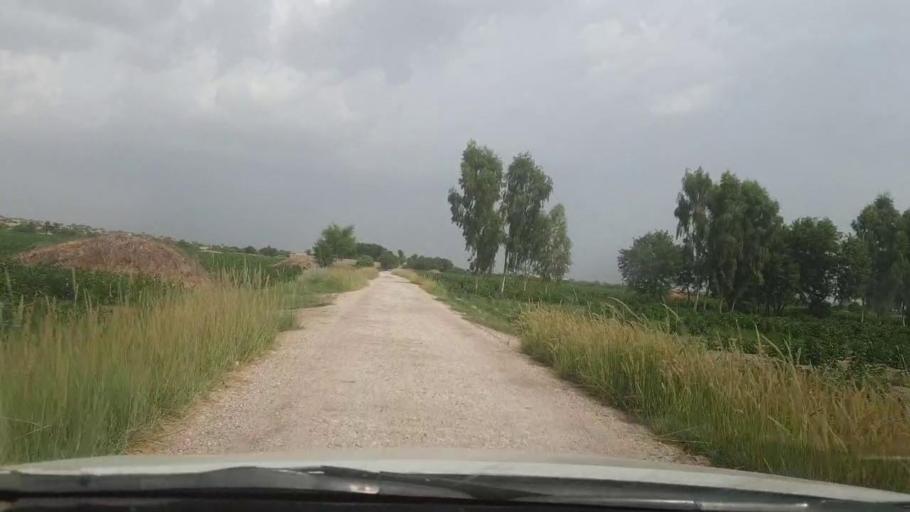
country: PK
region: Sindh
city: Kot Diji
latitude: 27.3375
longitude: 69.0344
